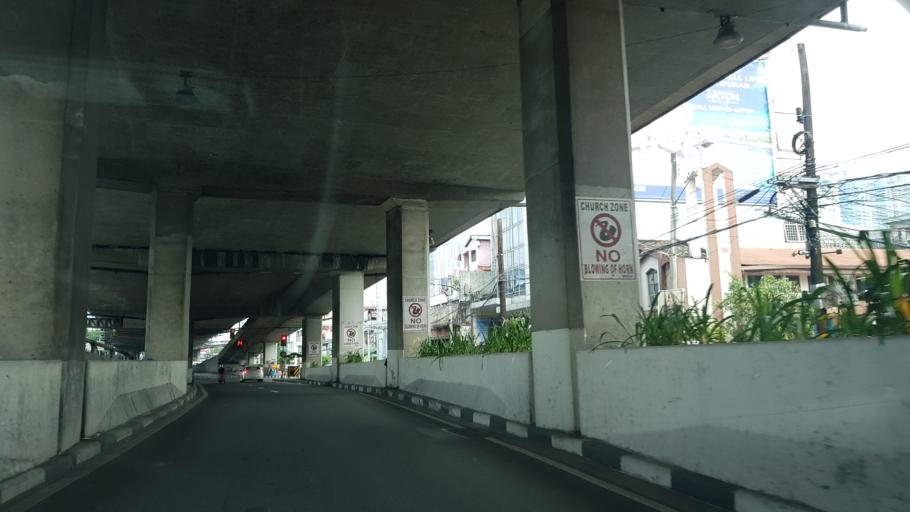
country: PH
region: Metro Manila
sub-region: Makati City
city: Makati City
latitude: 14.5574
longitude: 121.0394
